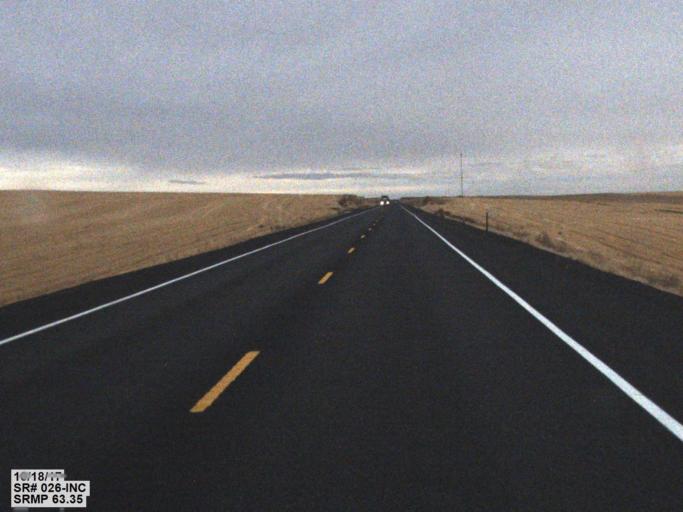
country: US
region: Washington
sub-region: Franklin County
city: Connell
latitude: 46.7944
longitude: -118.7001
